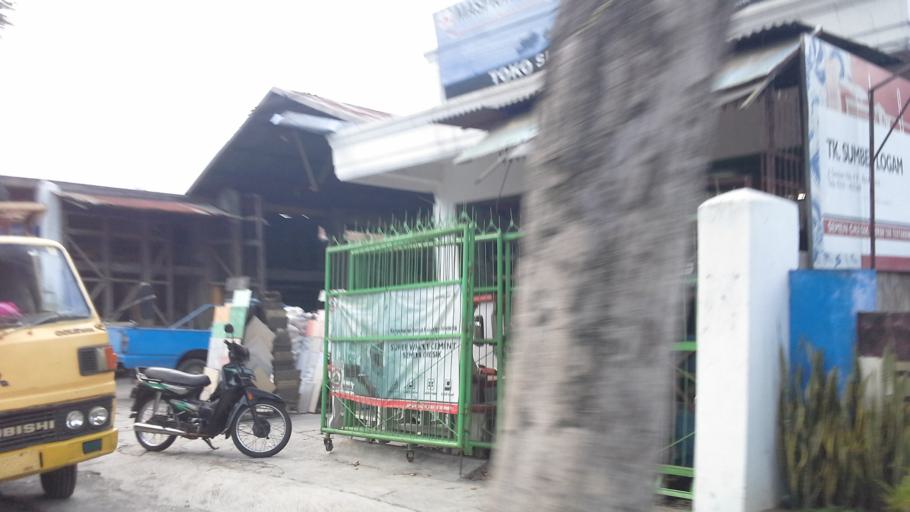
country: ID
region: East Java
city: Bondowoso
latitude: -7.9311
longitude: 113.8239
